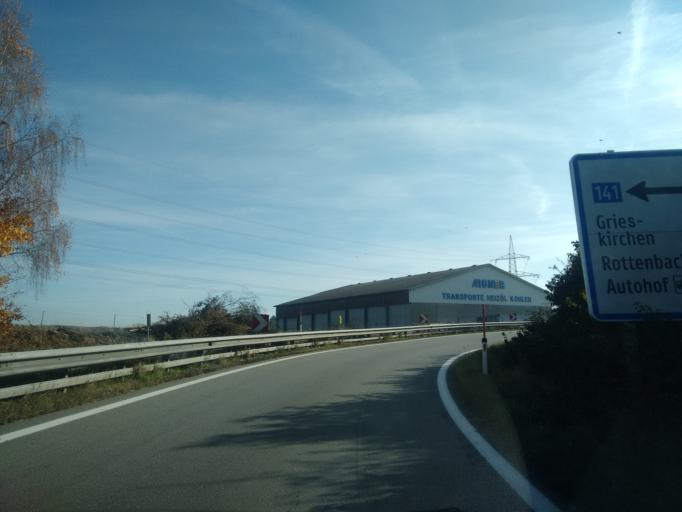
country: AT
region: Upper Austria
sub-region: Politischer Bezirk Vocklabruck
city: Wolfsegg am Hausruck
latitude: 48.2008
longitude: 13.6418
